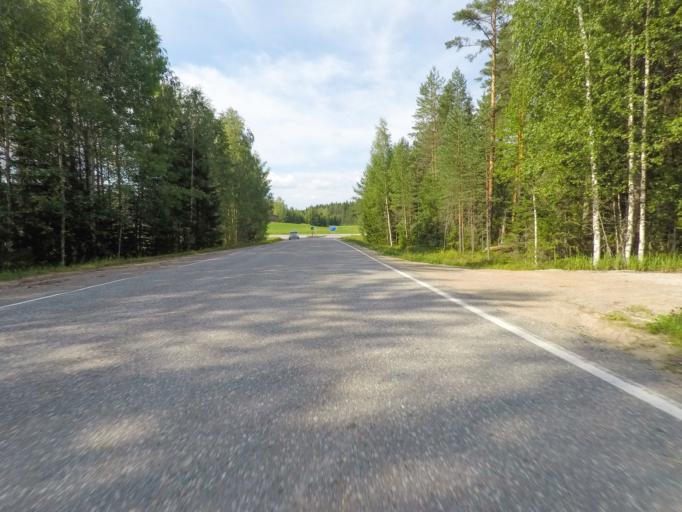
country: FI
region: Southern Savonia
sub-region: Savonlinna
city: Sulkava
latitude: 61.7895
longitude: 28.2429
